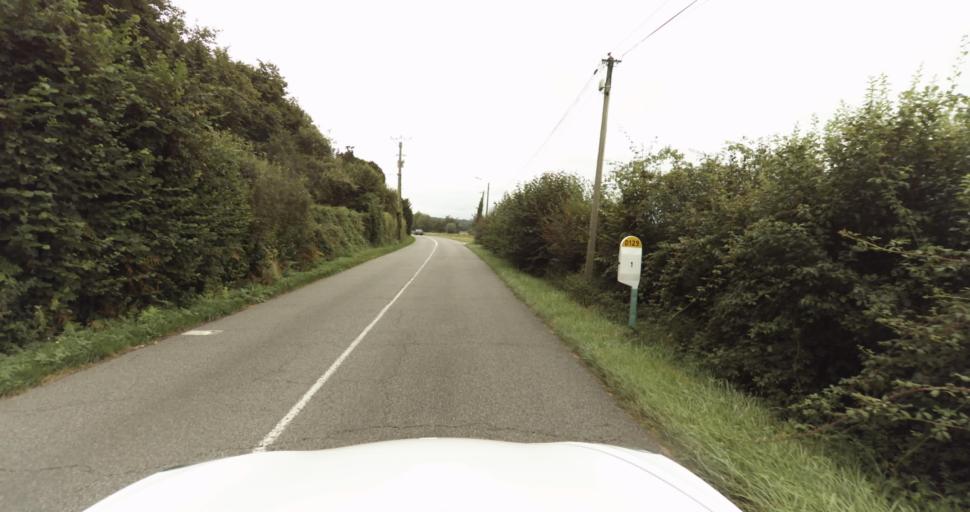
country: FR
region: Haute-Normandie
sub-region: Departement de l'Eure
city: Arnieres-sur-Iton
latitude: 49.0060
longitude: 1.1032
